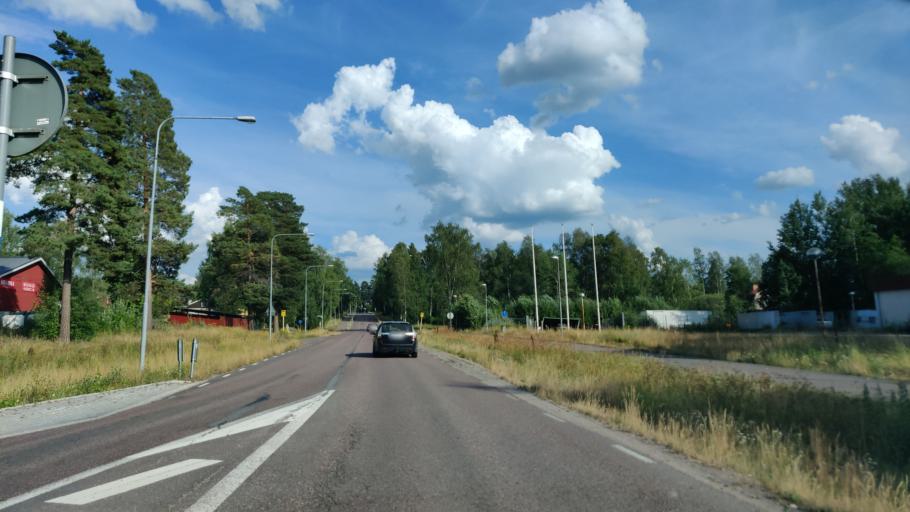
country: SE
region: Vaermland
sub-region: Hagfors Kommun
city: Hagfors
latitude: 60.0449
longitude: 13.6804
